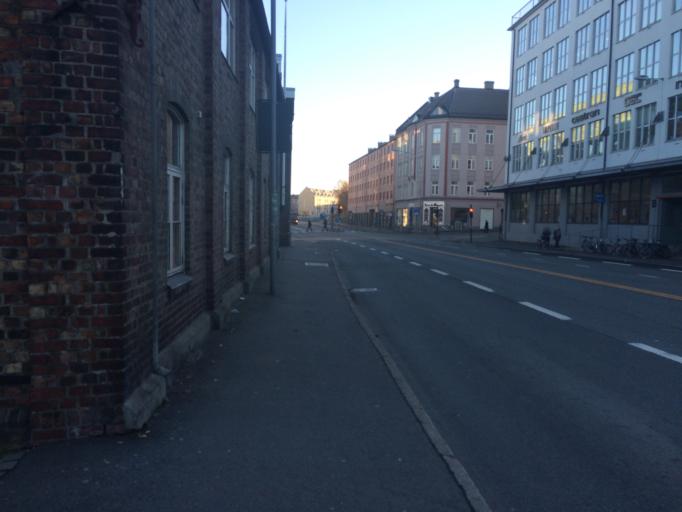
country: NO
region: Sor-Trondelag
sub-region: Trondheim
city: Trondheim
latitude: 63.4341
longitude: 10.4132
